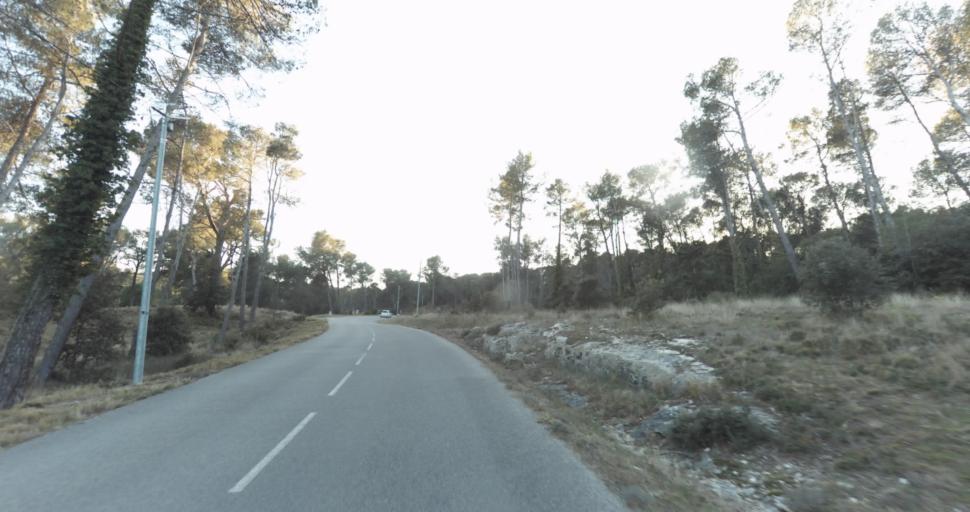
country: FR
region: Provence-Alpes-Cote d'Azur
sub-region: Departement des Bouches-du-Rhone
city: Barbentane
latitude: 43.8794
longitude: 4.7345
